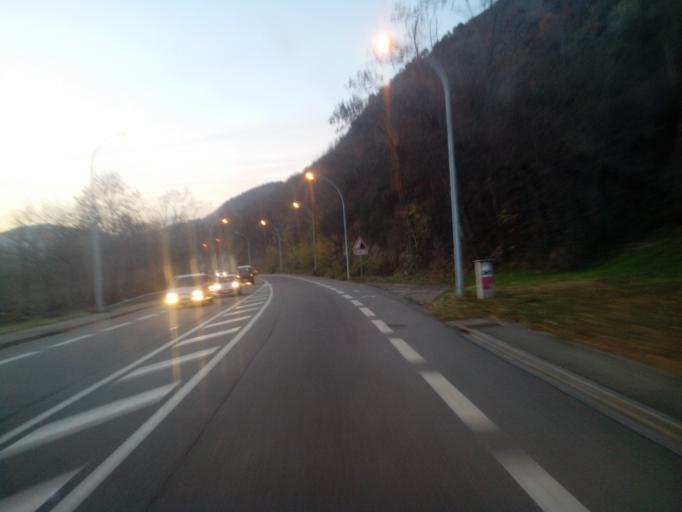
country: FR
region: Midi-Pyrenees
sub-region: Departement de l'Ariege
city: Montgaillard
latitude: 42.9562
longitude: 1.6231
